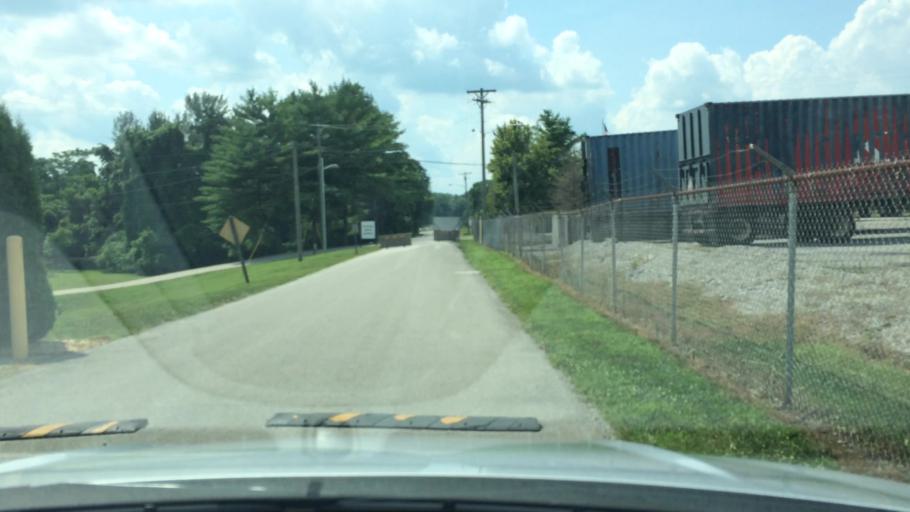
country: US
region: Kentucky
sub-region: Pulaski County
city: Somerset
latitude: 36.9703
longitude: -84.5855
